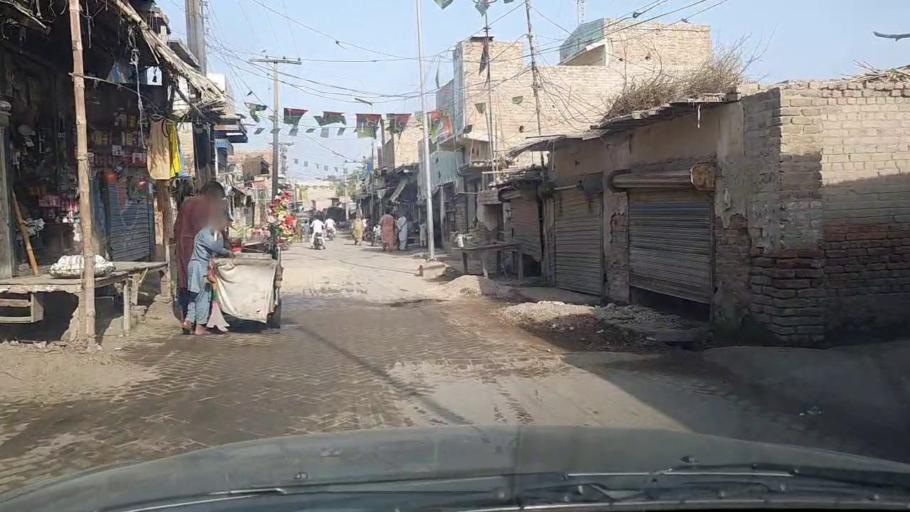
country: PK
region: Sindh
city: Pir jo Goth
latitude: 27.5570
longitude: 68.5538
